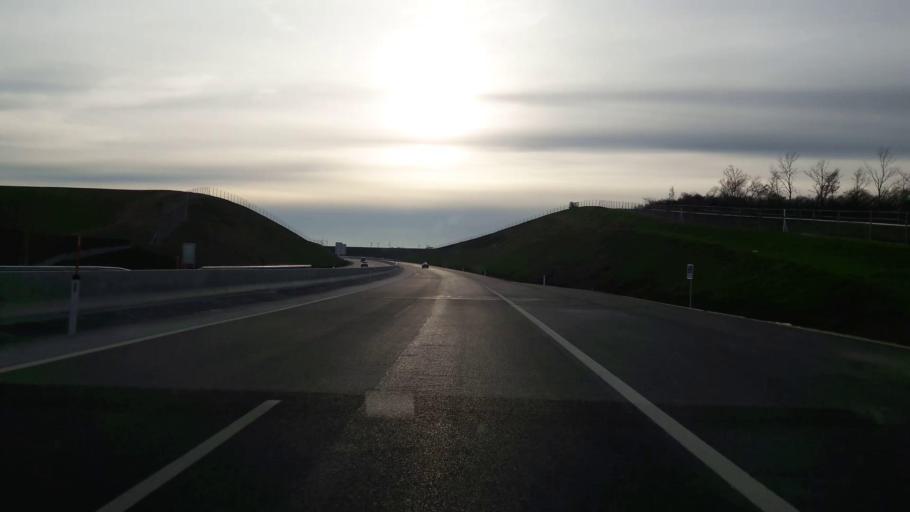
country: AT
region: Lower Austria
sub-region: Politischer Bezirk Mistelbach
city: Wilfersdorf
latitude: 48.5961
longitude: 16.6326
